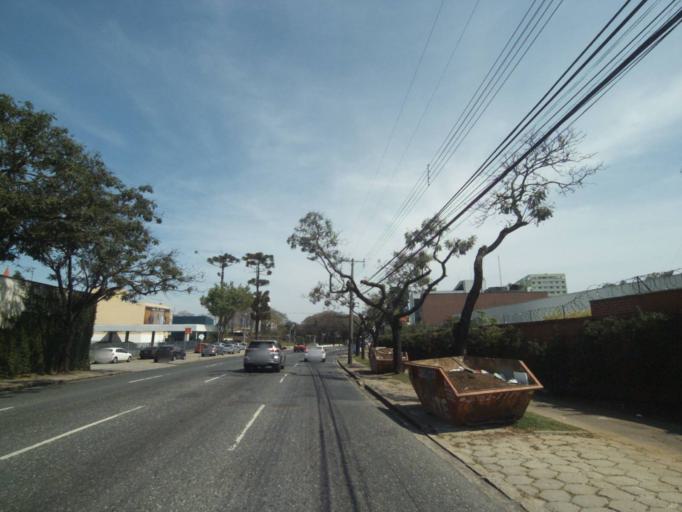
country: BR
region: Parana
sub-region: Curitiba
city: Curitiba
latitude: -25.4721
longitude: -49.2953
